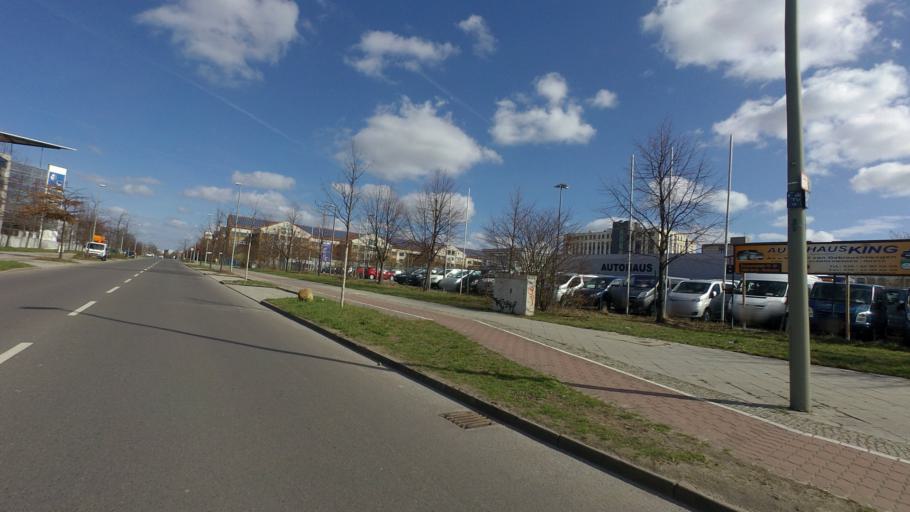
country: DE
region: Berlin
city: Falkenberg
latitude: 52.5580
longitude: 13.5489
